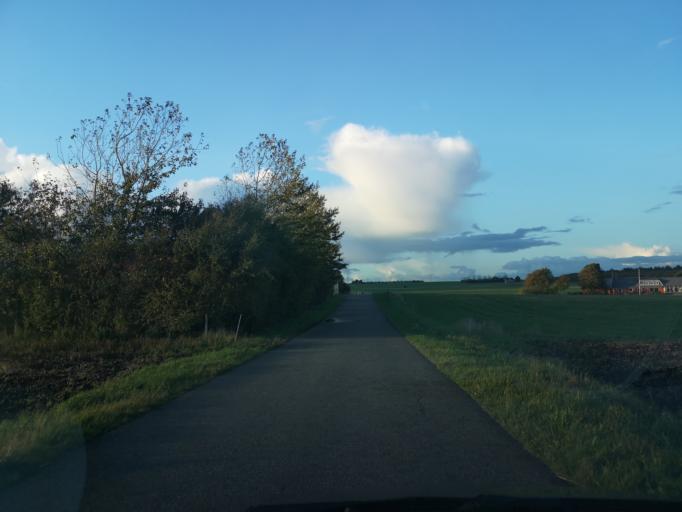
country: DK
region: Central Jutland
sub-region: Ringkobing-Skjern Kommune
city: Videbaek
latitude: 56.0421
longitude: 8.5805
